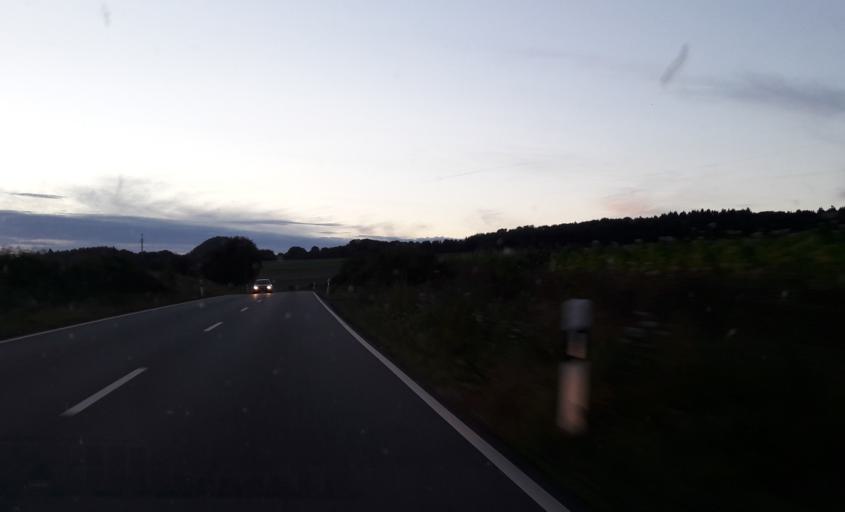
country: DE
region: Rheinland-Pfalz
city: Neuerburg
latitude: 49.9874
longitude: 6.9676
